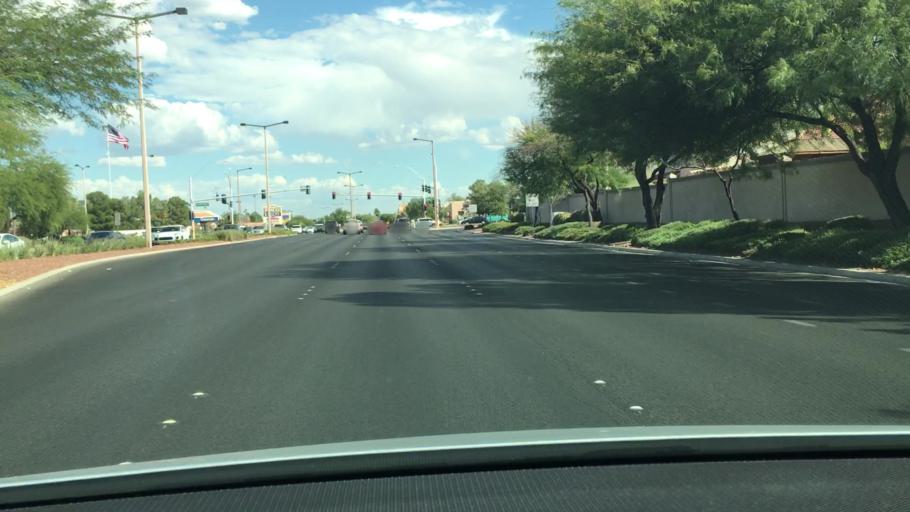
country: US
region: Nevada
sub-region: Clark County
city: Summerlin South
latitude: 36.2006
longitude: -115.2838
